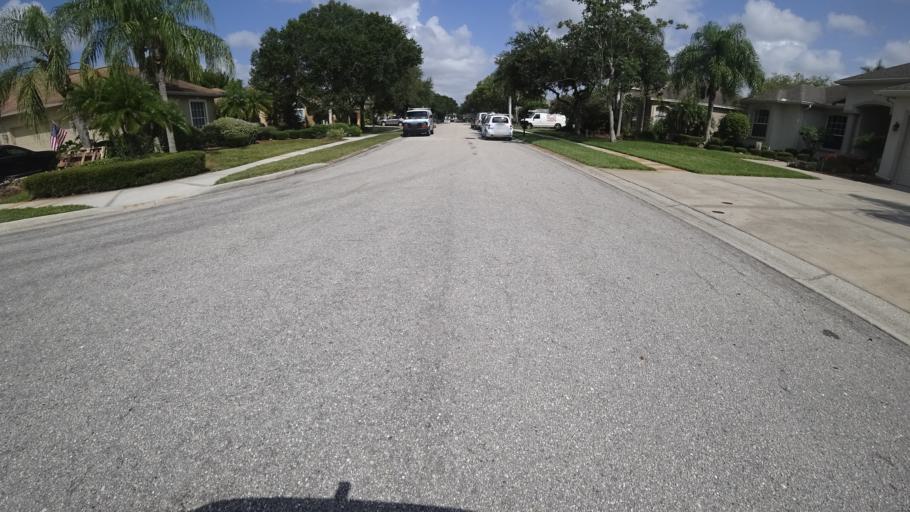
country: US
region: Florida
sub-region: Sarasota County
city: The Meadows
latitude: 27.4144
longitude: -82.4394
